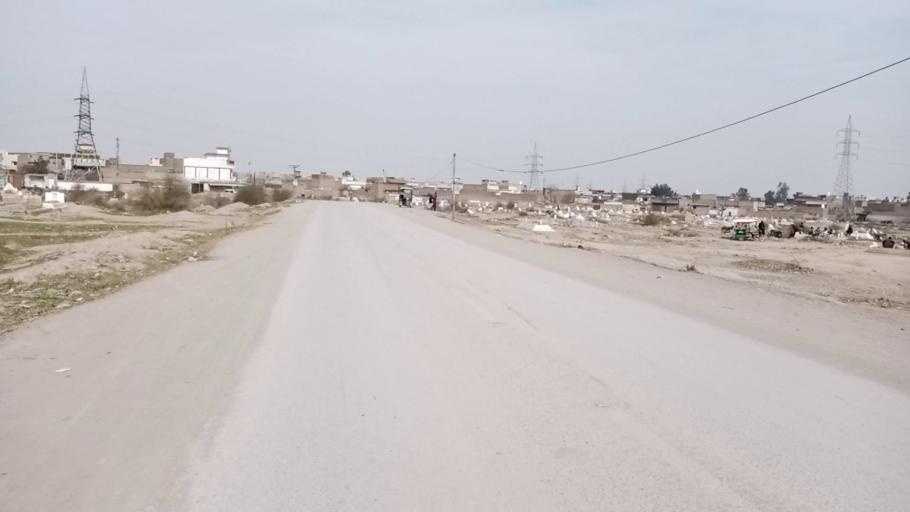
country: PK
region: Khyber Pakhtunkhwa
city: Peshawar
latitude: 33.9847
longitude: 71.4679
